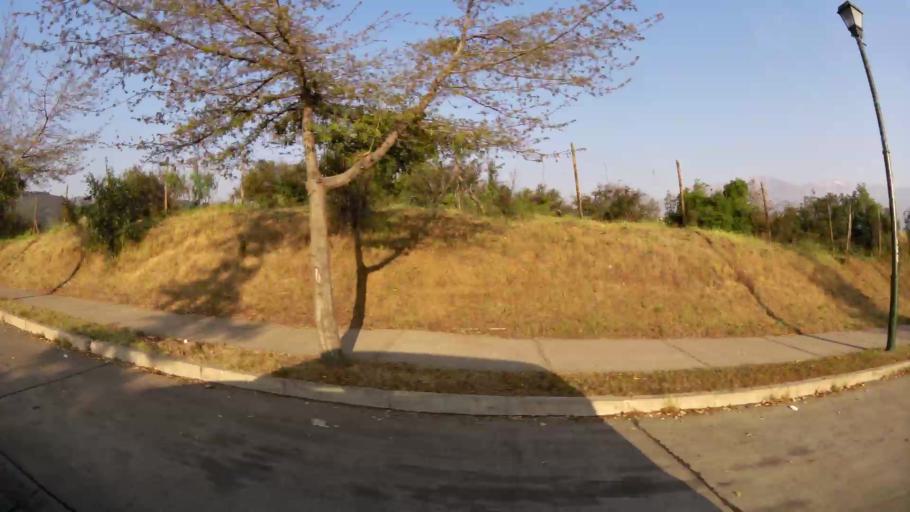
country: CL
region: Santiago Metropolitan
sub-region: Provincia de Santiago
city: Villa Presidente Frei, Nunoa, Santiago, Chile
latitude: -33.3343
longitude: -70.5071
